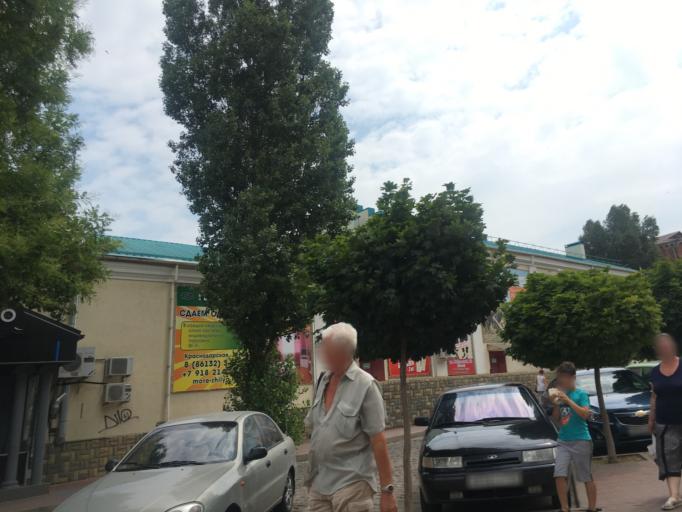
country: RU
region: Krasnodarskiy
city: Yeysk
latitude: 46.7119
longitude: 38.2755
